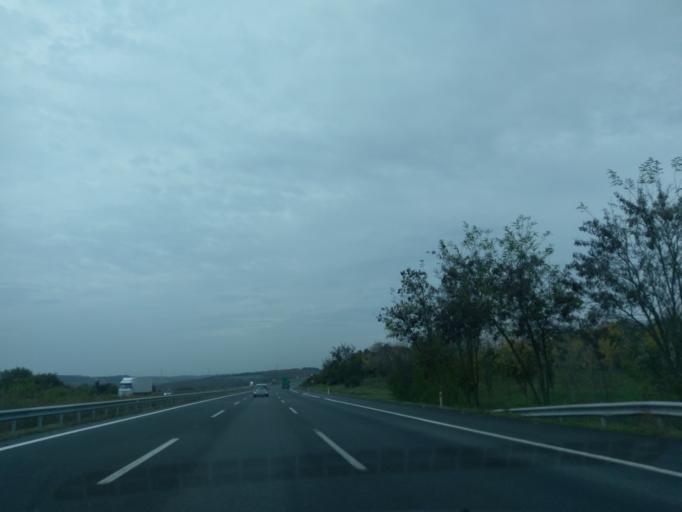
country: TR
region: Istanbul
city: Canta
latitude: 41.1704
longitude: 28.1212
